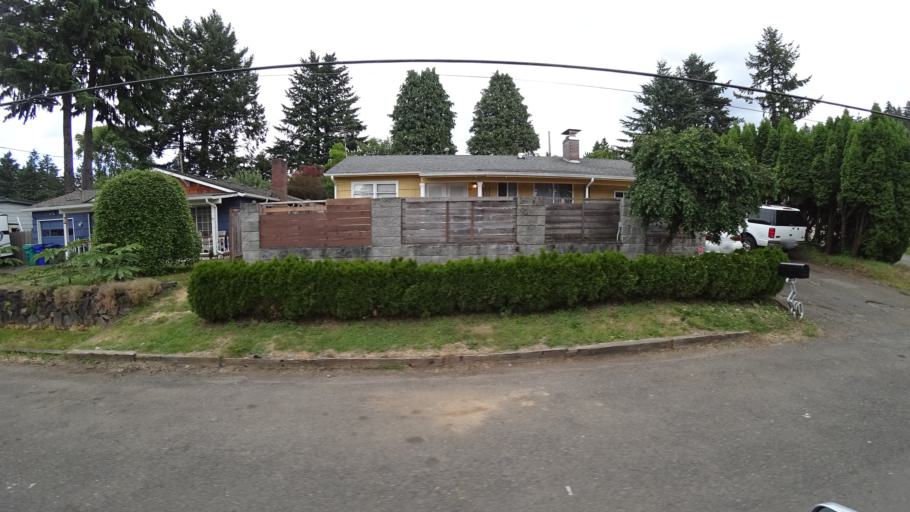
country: US
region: Oregon
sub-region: Clackamas County
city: Happy Valley
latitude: 45.4953
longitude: -122.5097
